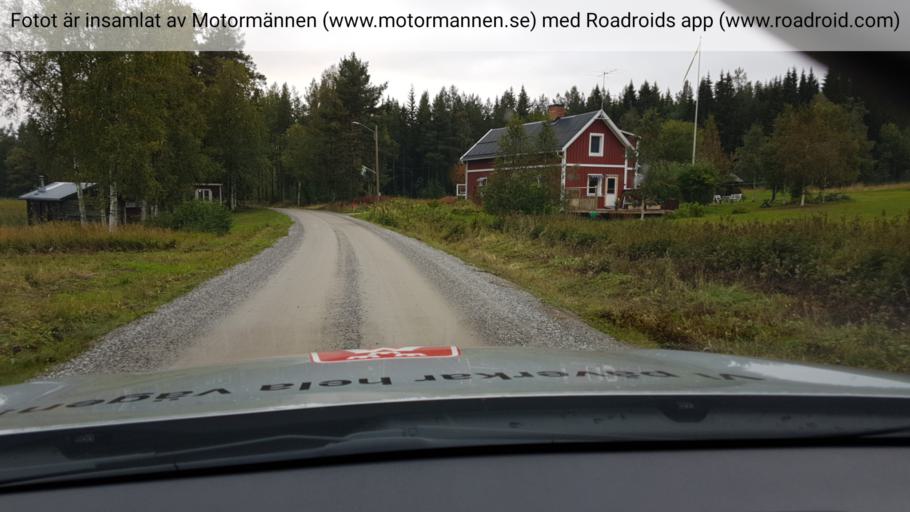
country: SE
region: Jaemtland
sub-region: Braecke Kommun
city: Braecke
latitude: 62.7487
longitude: 15.5030
